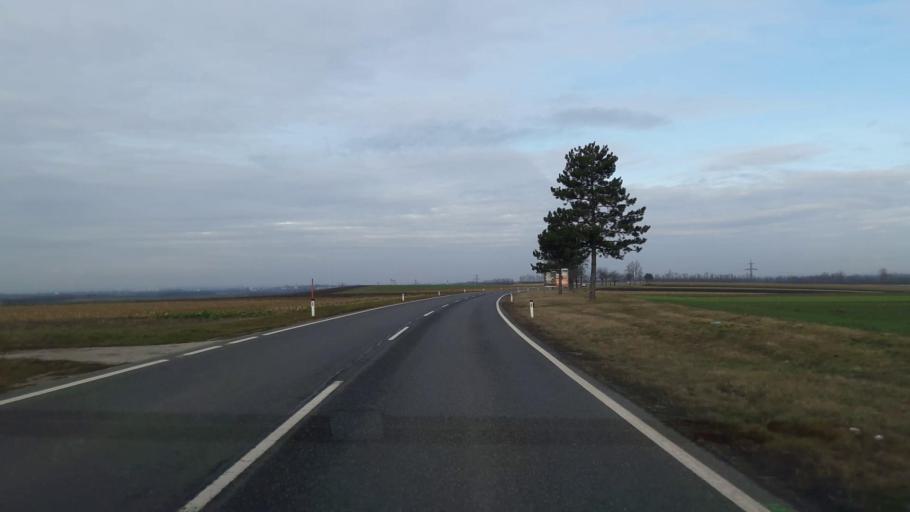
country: AT
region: Lower Austria
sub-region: Politischer Bezirk Mistelbach
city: Staatz
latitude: 48.6955
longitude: 16.4465
